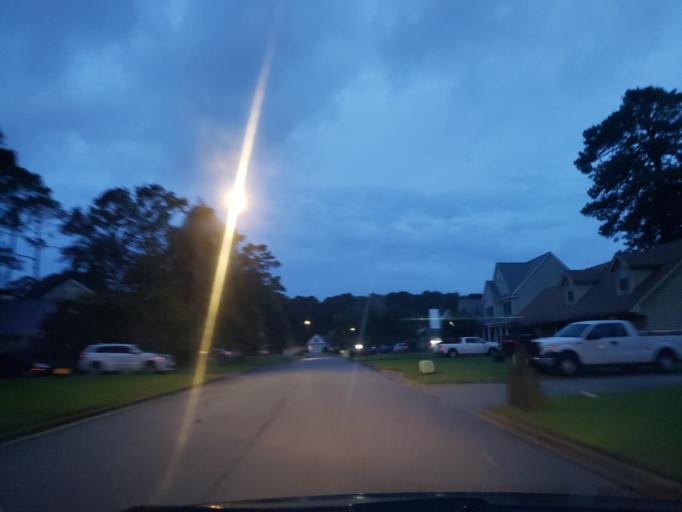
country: US
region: Georgia
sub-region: Chatham County
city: Isle of Hope
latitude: 31.9833
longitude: -81.0784
